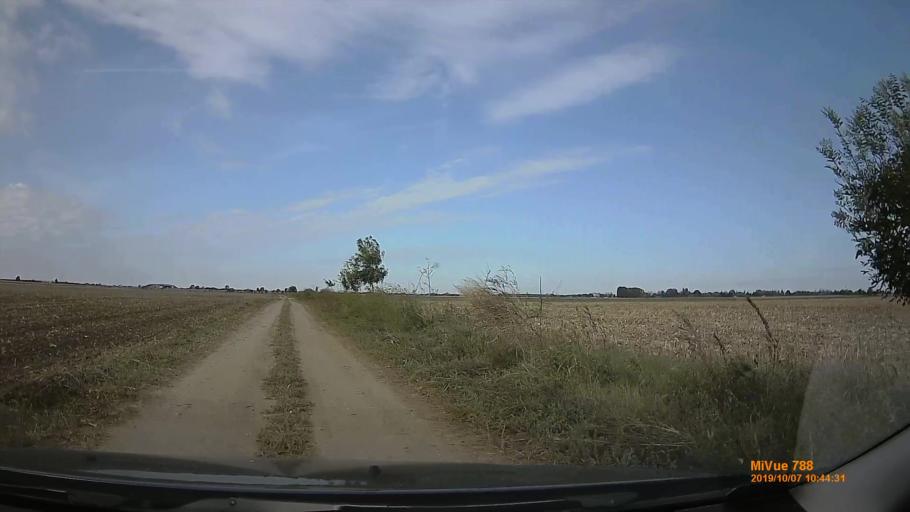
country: HU
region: Bekes
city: Kondoros
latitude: 46.7346
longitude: 20.8294
